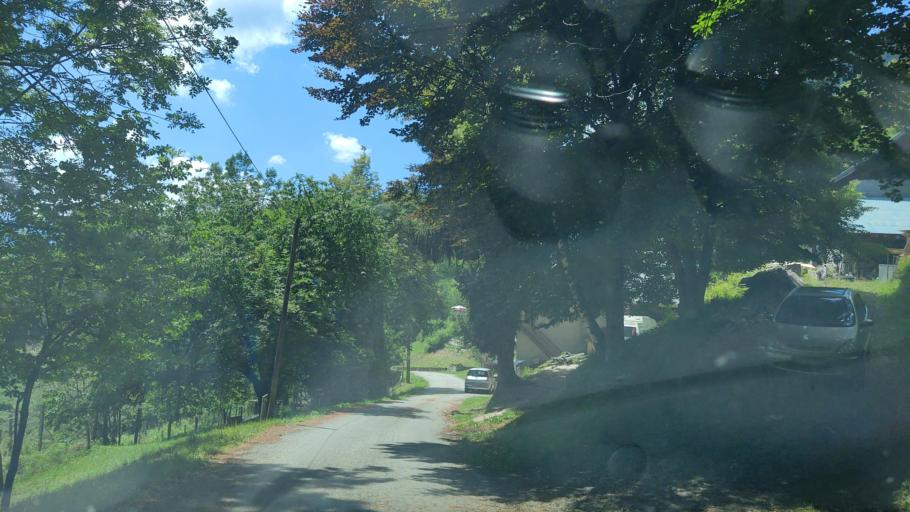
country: FR
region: Rhone-Alpes
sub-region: Departement de la Savoie
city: Aiton
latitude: 45.5122
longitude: 6.2880
